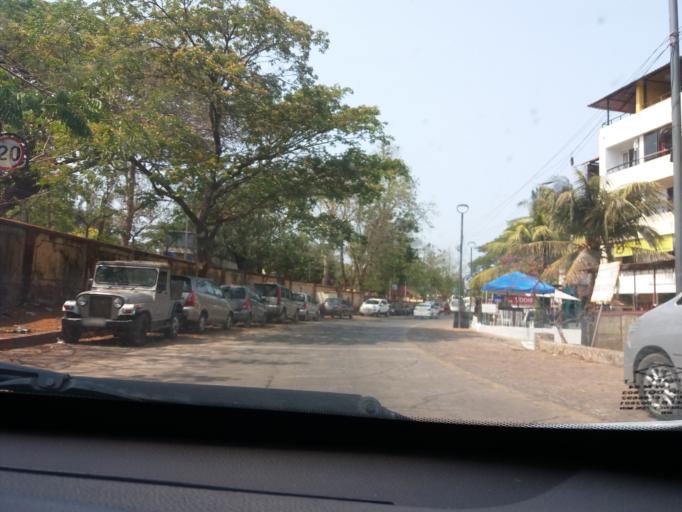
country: IN
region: Goa
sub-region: North Goa
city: Taleigao
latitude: 15.4561
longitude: 73.8030
